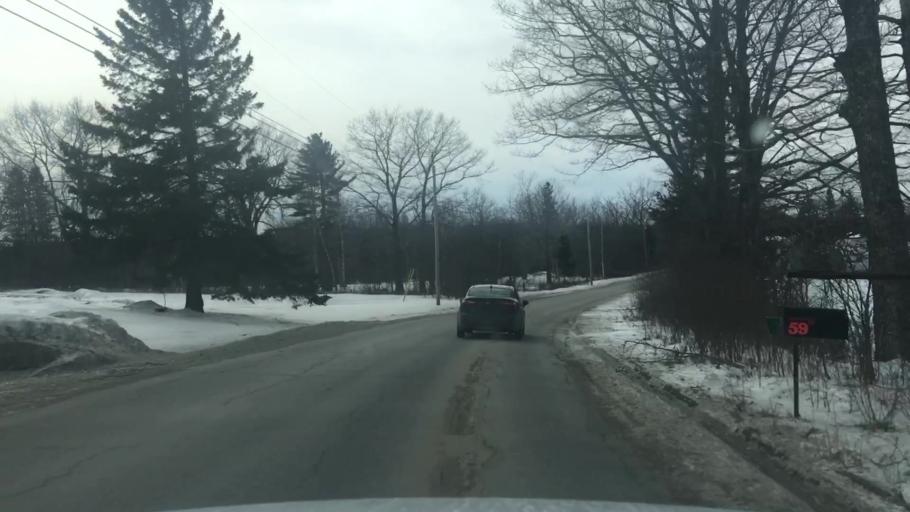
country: US
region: Maine
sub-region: Hancock County
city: Orland
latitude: 44.5765
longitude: -68.7264
